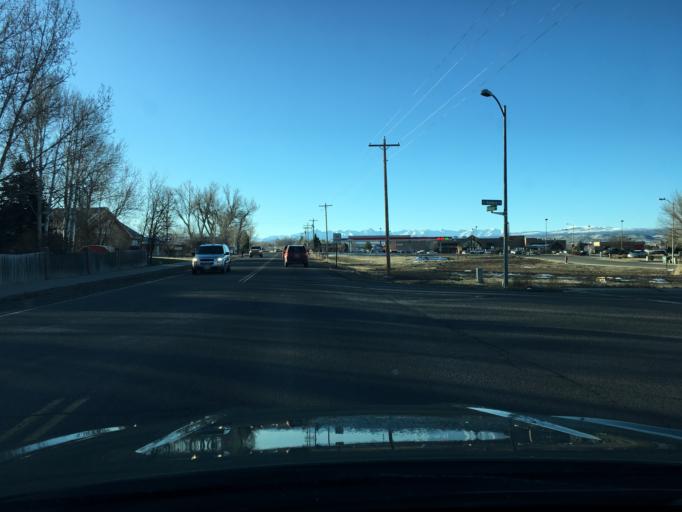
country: US
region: Colorado
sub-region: Montrose County
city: Montrose
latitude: 38.4560
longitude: -107.8649
